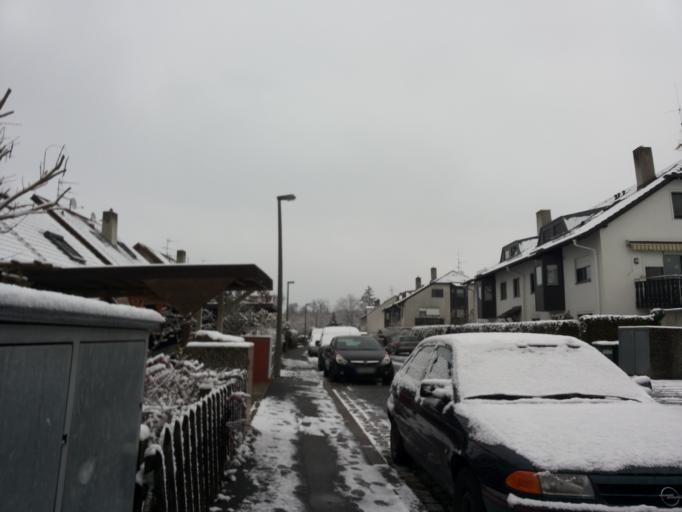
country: DE
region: Bavaria
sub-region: Regierungsbezirk Mittelfranken
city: Rosstal
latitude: 49.4278
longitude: 10.9048
